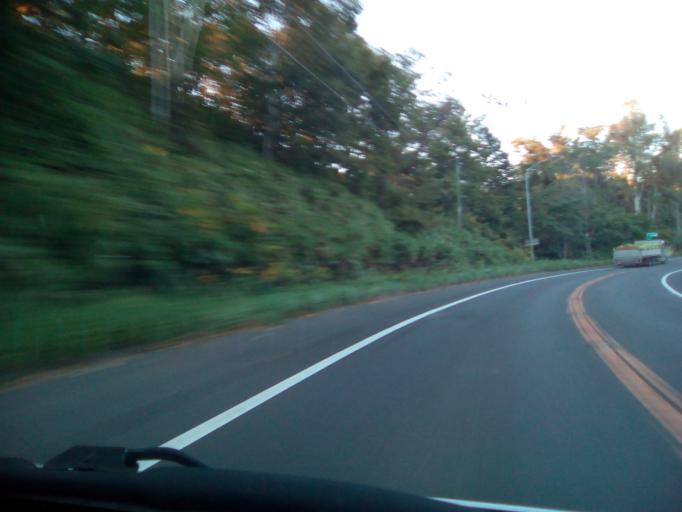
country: JP
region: Hokkaido
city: Niseko Town
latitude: 42.6918
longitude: 140.8340
